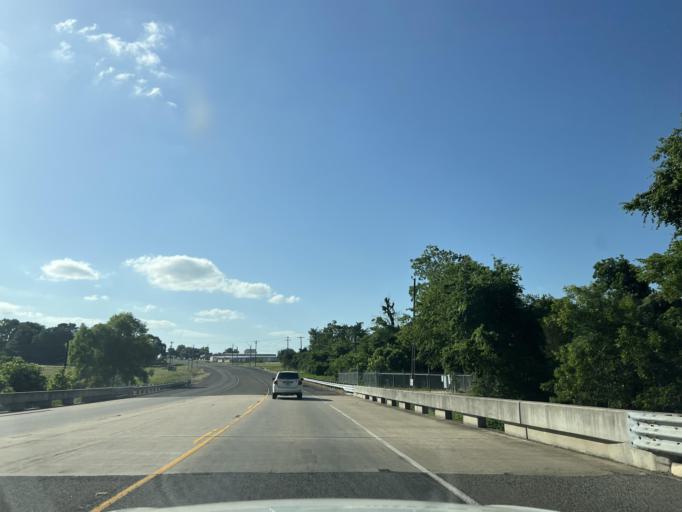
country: US
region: Texas
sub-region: Washington County
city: Brenham
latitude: 30.1547
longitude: -96.3694
